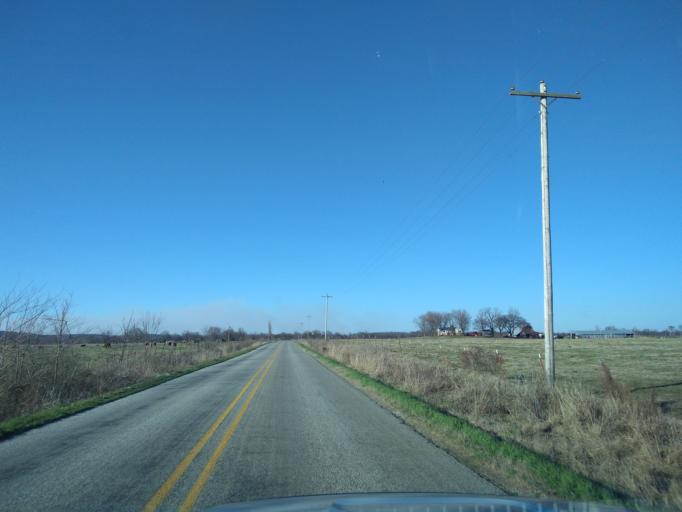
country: US
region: Arkansas
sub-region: Washington County
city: Lincoln
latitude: 36.0100
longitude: -94.3926
